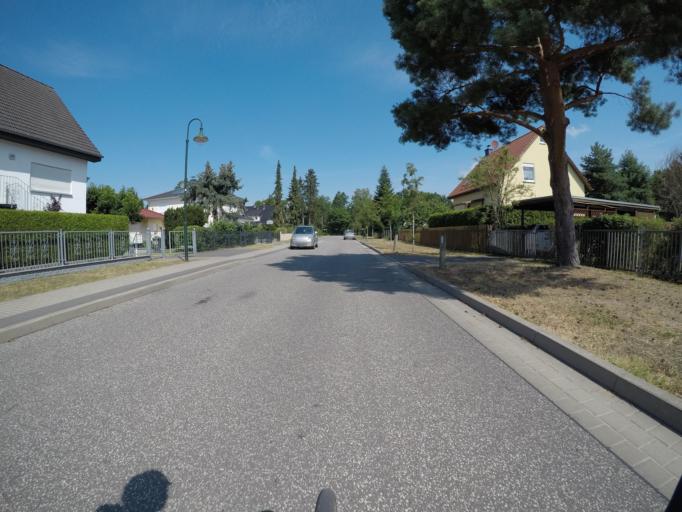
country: DE
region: Brandenburg
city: Bernau bei Berlin
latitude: 52.6807
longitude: 13.5671
